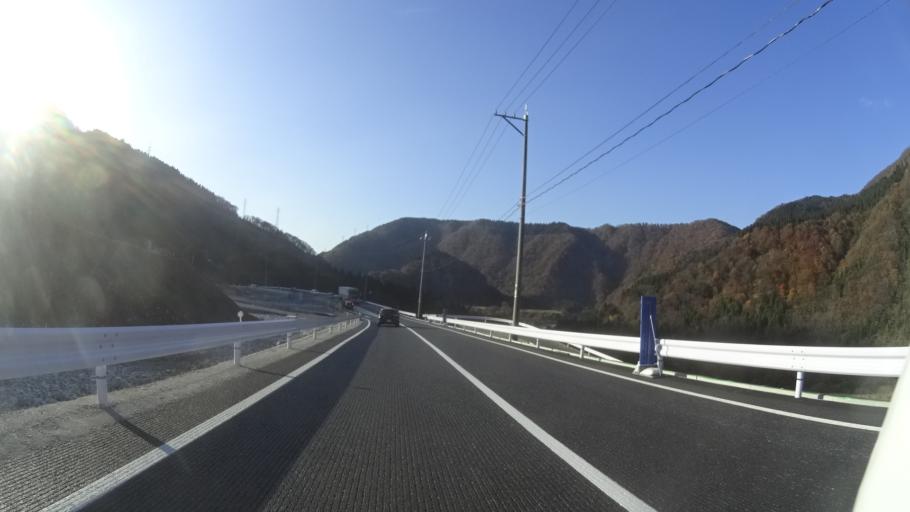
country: JP
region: Fukui
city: Ono
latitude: 35.9648
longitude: 136.6041
